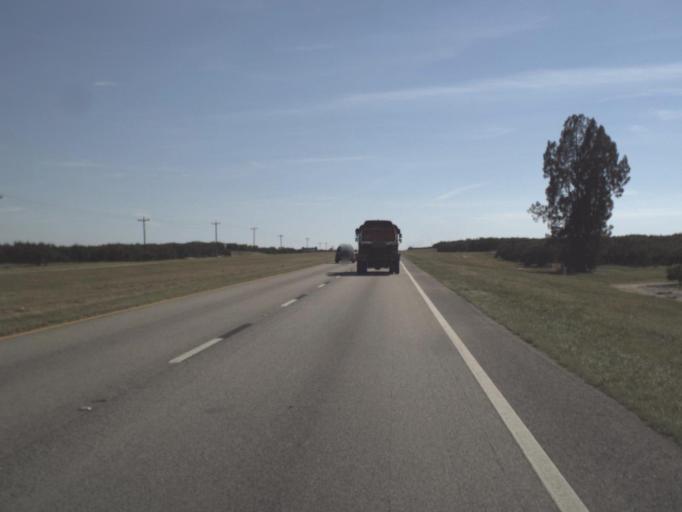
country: US
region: Florida
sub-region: Highlands County
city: Placid Lakes
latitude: 27.1964
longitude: -81.3288
